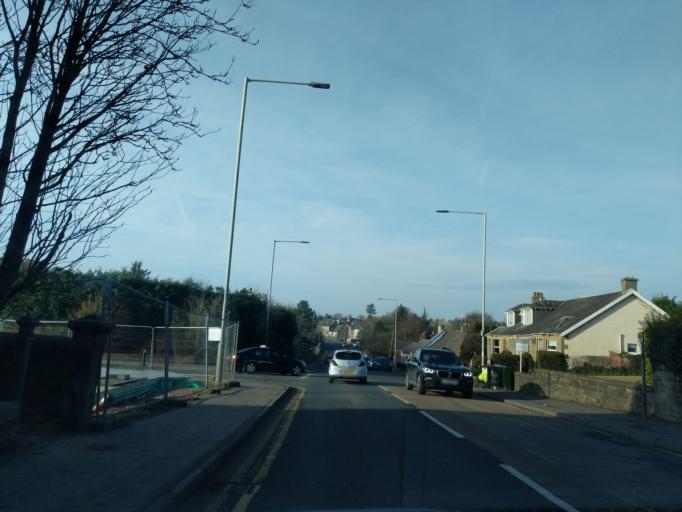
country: GB
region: Scotland
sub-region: South Lanarkshire
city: Carluke
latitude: 55.7297
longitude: -3.8364
